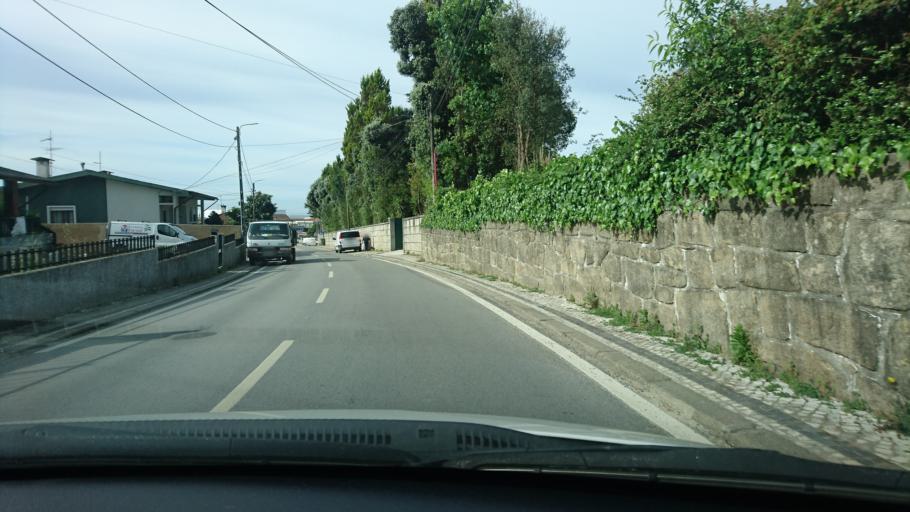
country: PT
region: Aveiro
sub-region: Oliveira de Azemeis
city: Oliveira de Azemeis
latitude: 40.8555
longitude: -8.4785
